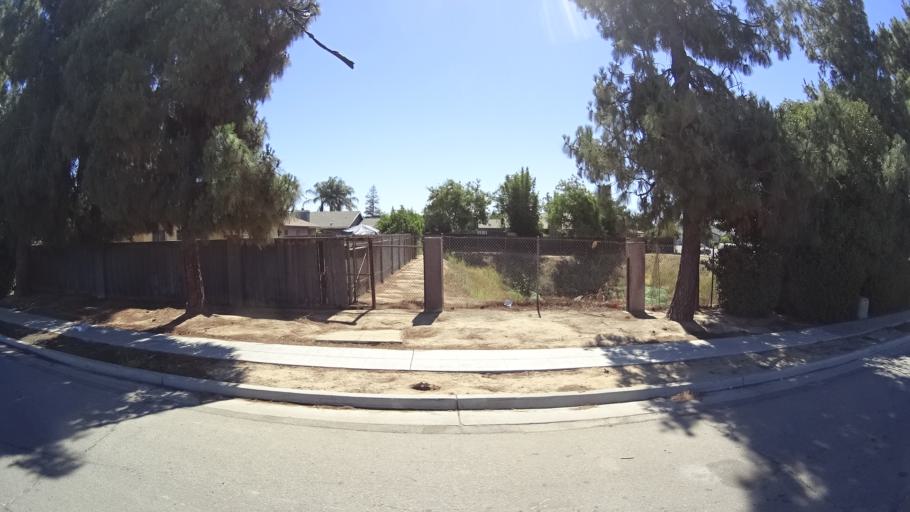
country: US
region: California
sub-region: Fresno County
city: Easton
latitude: 36.6976
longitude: -119.7998
